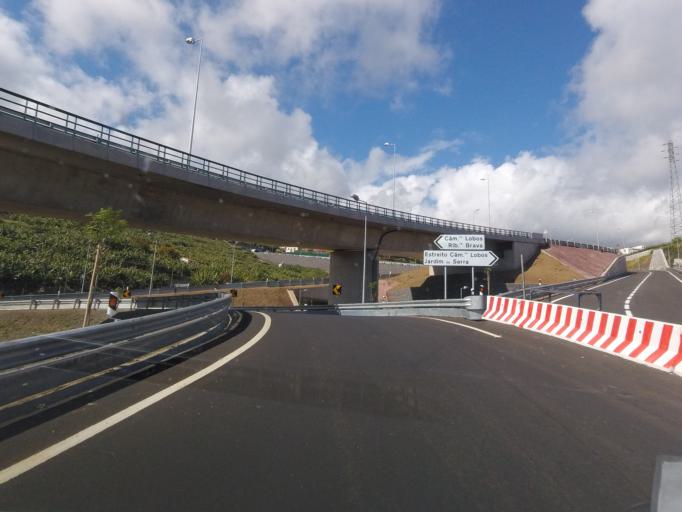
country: PT
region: Madeira
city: Camara de Lobos
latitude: 32.6598
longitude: -16.9692
